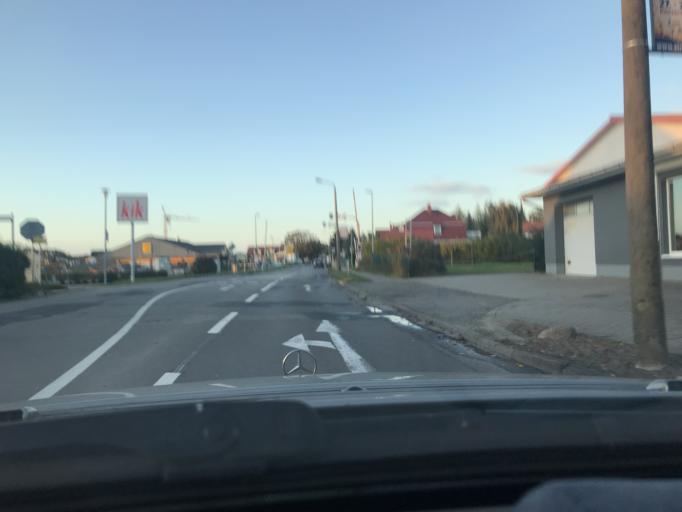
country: DE
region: Mecklenburg-Vorpommern
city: Ostseebad Zinnowitz
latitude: 54.0730
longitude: 13.9092
